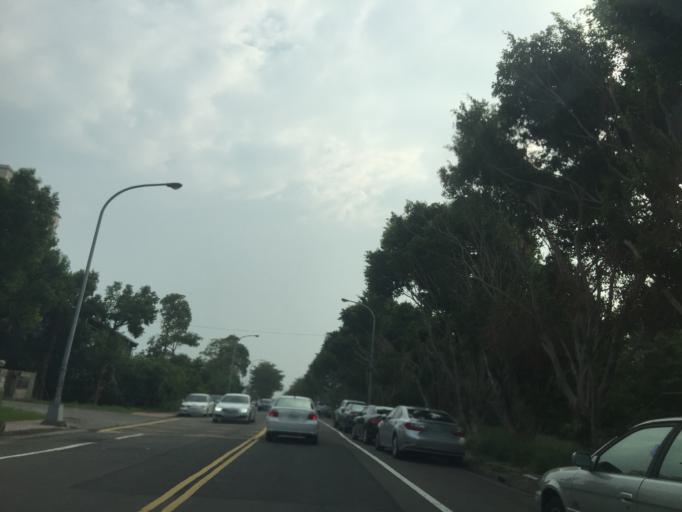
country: TW
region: Taiwan
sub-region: Hsinchu
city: Zhubei
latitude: 24.8201
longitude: 121.0154
